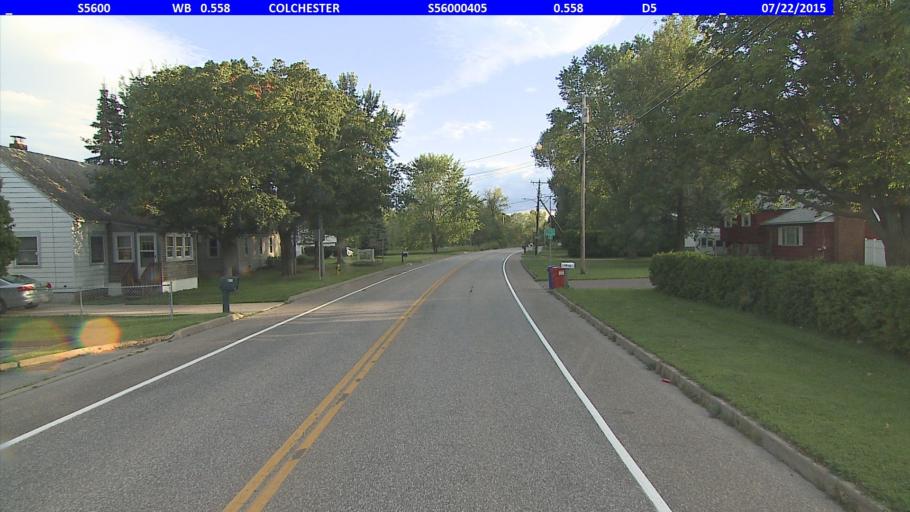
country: US
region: Vermont
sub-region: Chittenden County
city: Burlington
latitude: 44.5320
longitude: -73.2512
